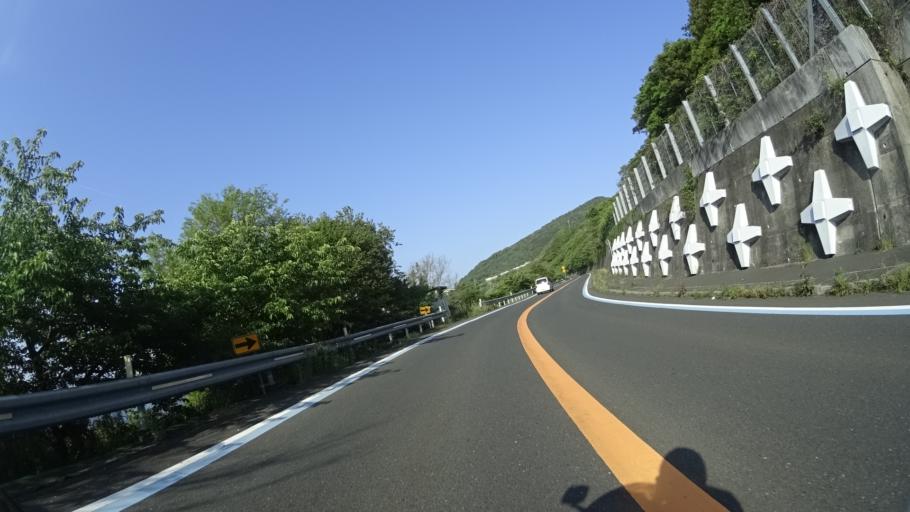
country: JP
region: Ehime
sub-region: Nishiuwa-gun
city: Ikata-cho
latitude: 33.3984
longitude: 132.1642
